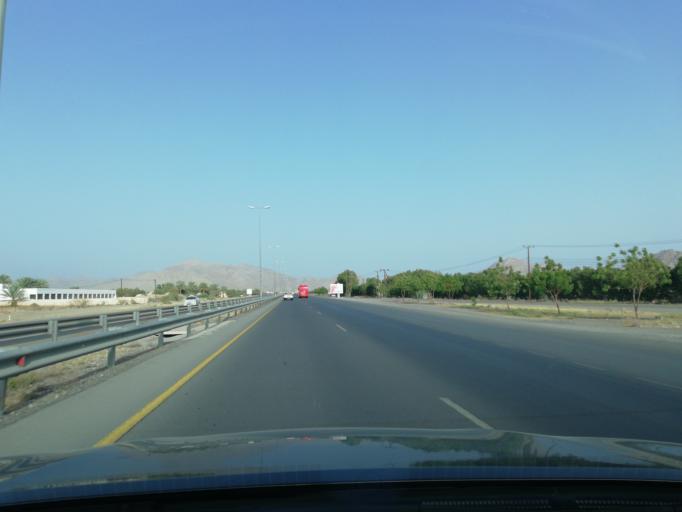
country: OM
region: Muhafazat ad Dakhiliyah
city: Nizwa
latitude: 22.8602
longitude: 57.5569
